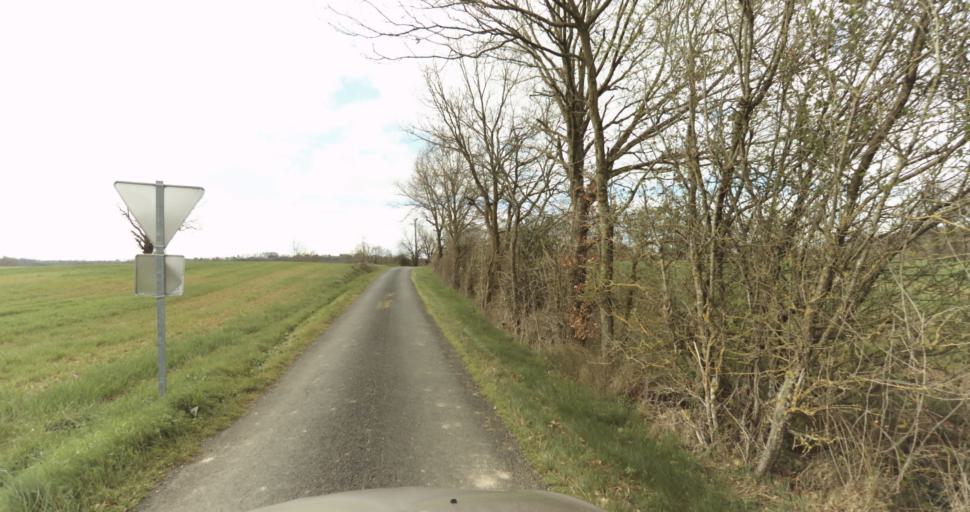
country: FR
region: Midi-Pyrenees
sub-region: Departement du Tarn
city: Frejairolles
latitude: 43.8832
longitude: 2.2000
